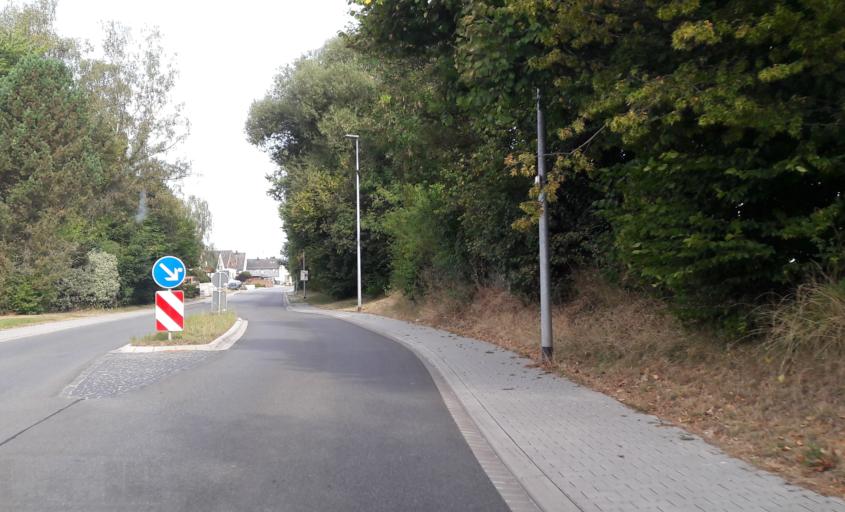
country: DE
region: Rheinland-Pfalz
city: Ellenberg
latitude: 49.6512
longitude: 7.1571
